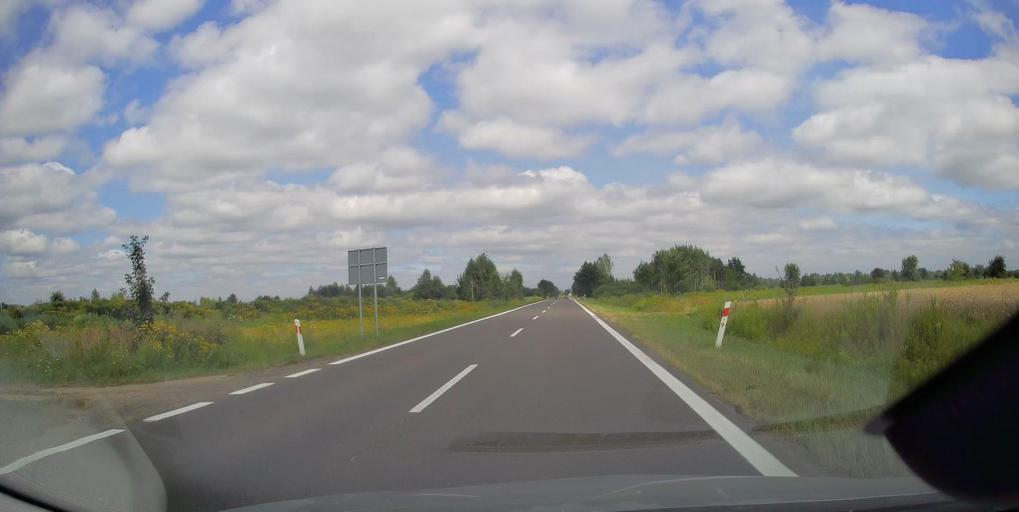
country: PL
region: Subcarpathian Voivodeship
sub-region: Powiat tarnobrzeski
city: Baranow Sandomierski
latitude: 50.4916
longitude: 21.5696
